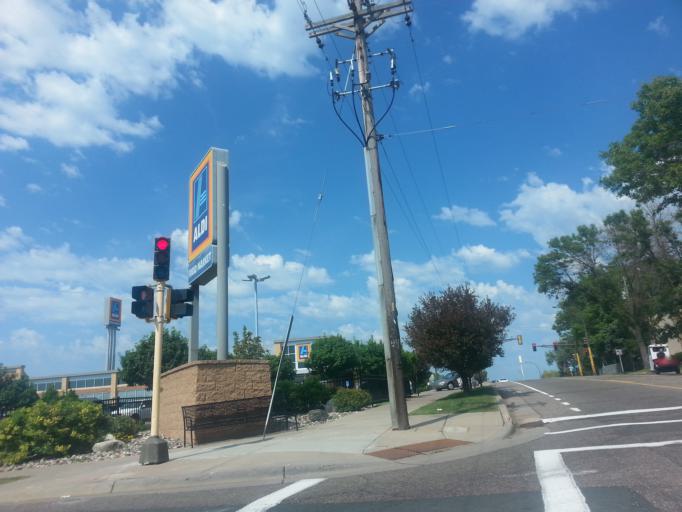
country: US
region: Minnesota
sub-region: Ramsey County
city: Maplewood
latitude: 44.9499
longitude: -93.0152
